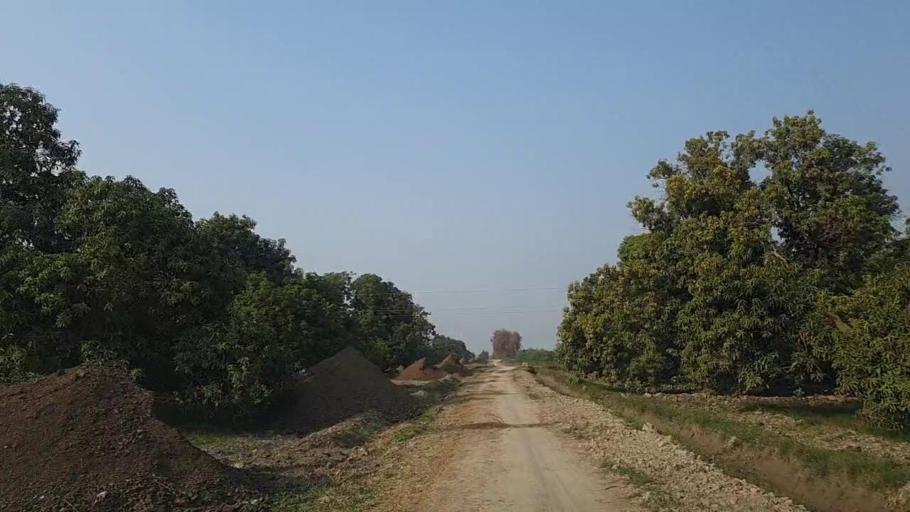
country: PK
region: Sindh
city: Sann
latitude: 26.1089
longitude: 68.1616
